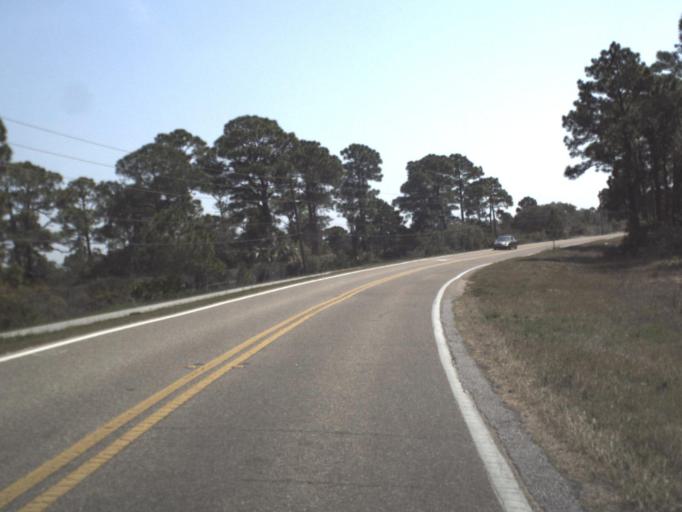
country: US
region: Florida
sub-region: Gulf County
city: Port Saint Joe
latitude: 29.6766
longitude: -85.3556
